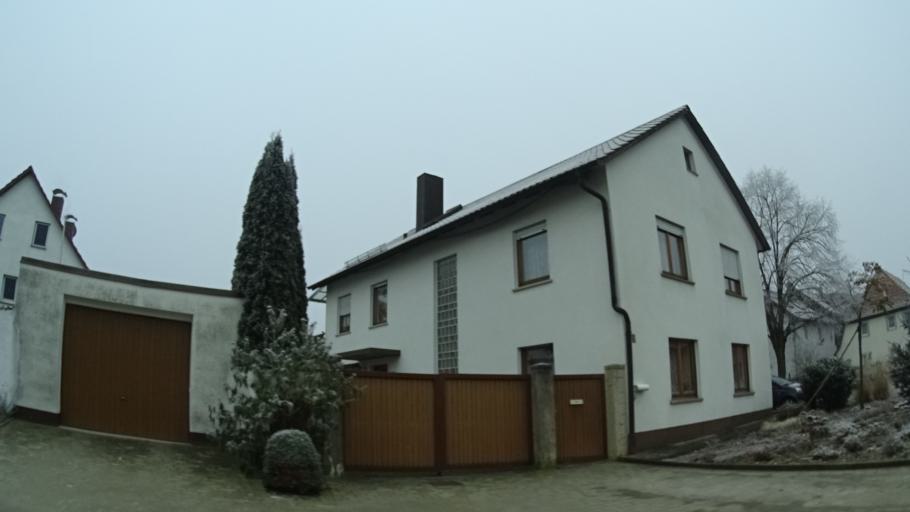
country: DE
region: Bavaria
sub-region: Regierungsbezirk Unterfranken
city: Lulsfeld
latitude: 49.8690
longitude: 10.3191
